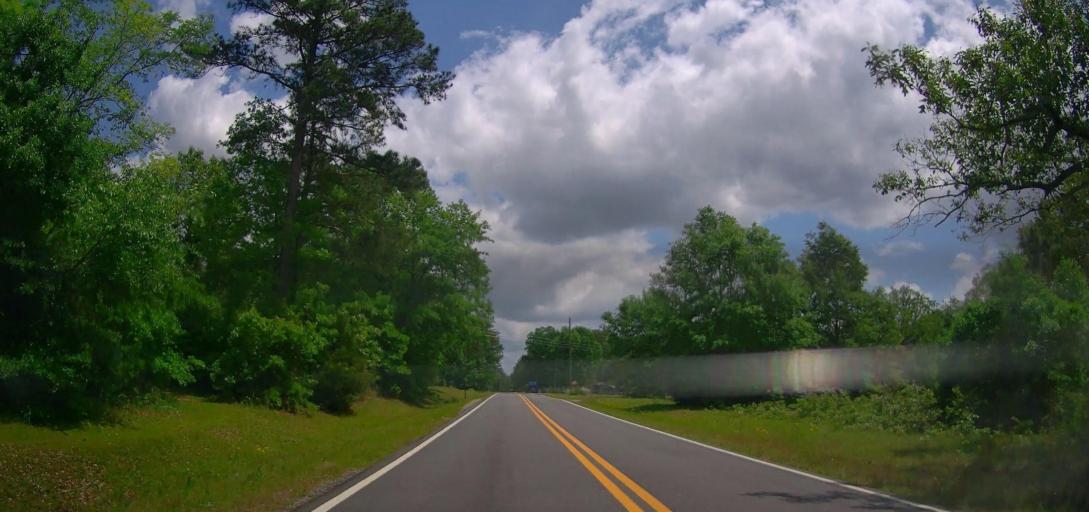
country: US
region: Georgia
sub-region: Laurens County
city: Dublin
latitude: 32.6034
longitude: -82.9381
